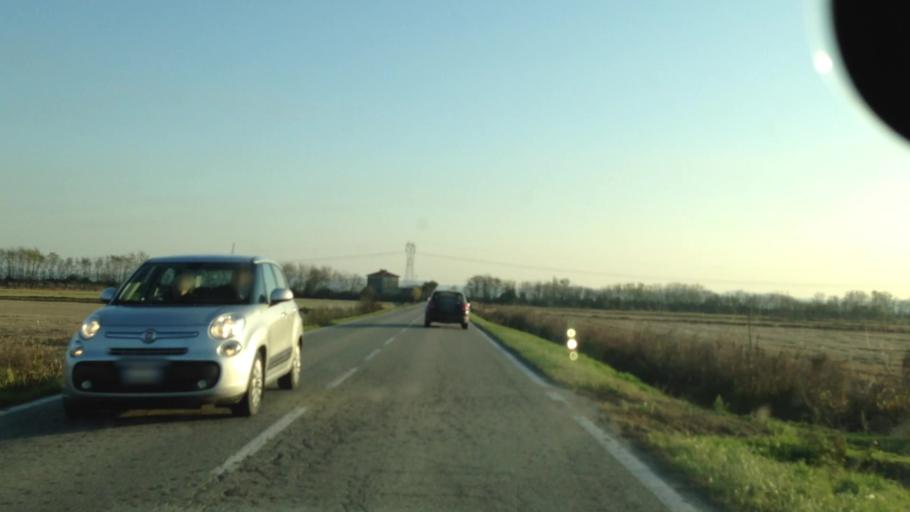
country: IT
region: Piedmont
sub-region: Provincia di Vercelli
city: Lamporo
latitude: 45.2491
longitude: 8.0890
